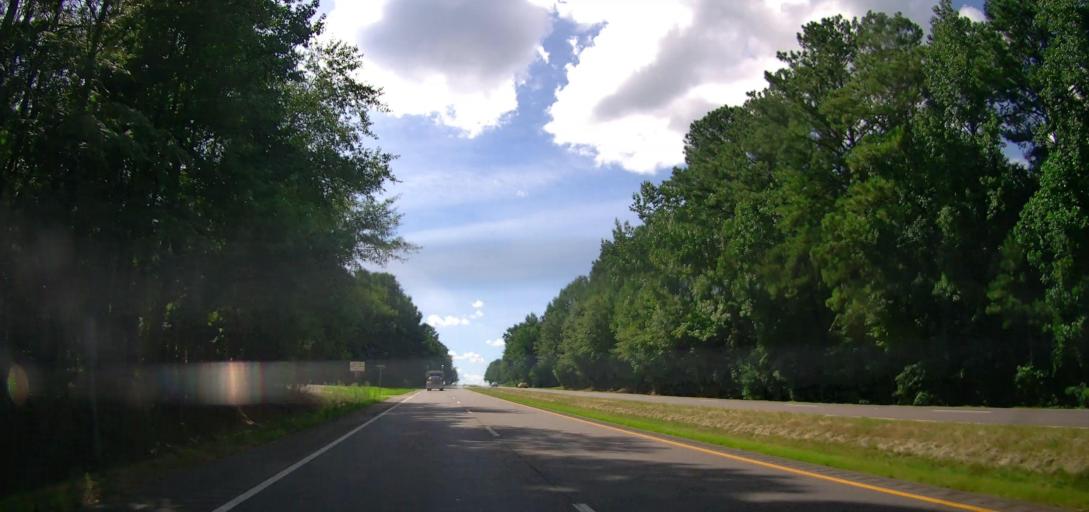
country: US
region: Alabama
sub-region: Tuscaloosa County
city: Northport
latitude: 33.2491
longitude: -87.6808
